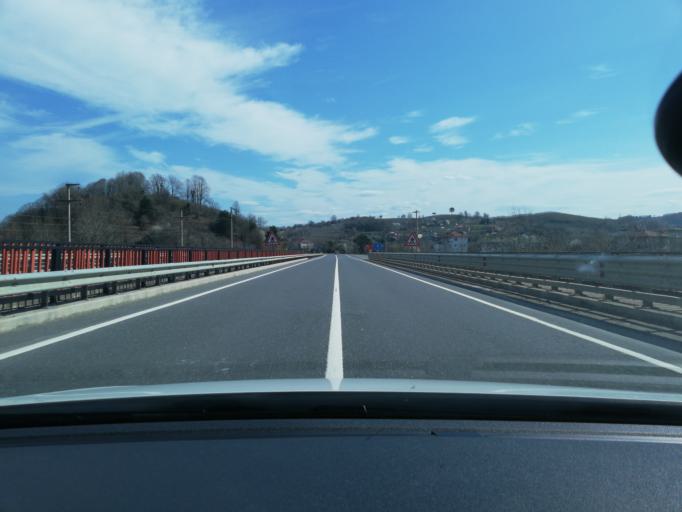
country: TR
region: Duzce
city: Akcakoca
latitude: 41.0965
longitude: 31.2141
